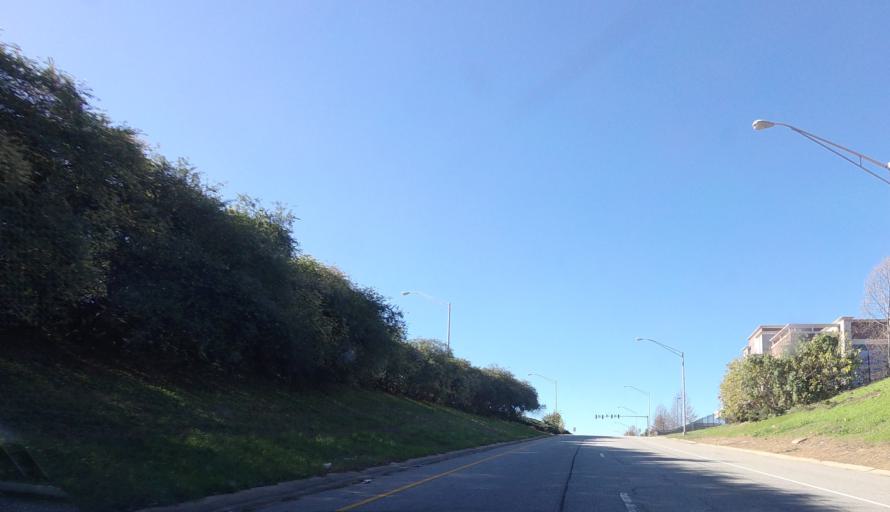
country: US
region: Georgia
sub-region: Fulton County
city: Atlanta
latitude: 33.7454
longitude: -84.3990
